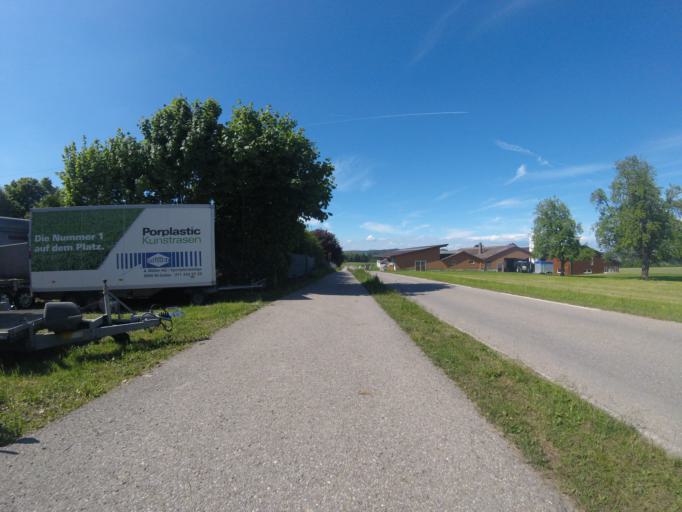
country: CH
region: Saint Gallen
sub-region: Wahlkreis Wil
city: Jonschwil
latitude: 47.4246
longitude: 9.0621
